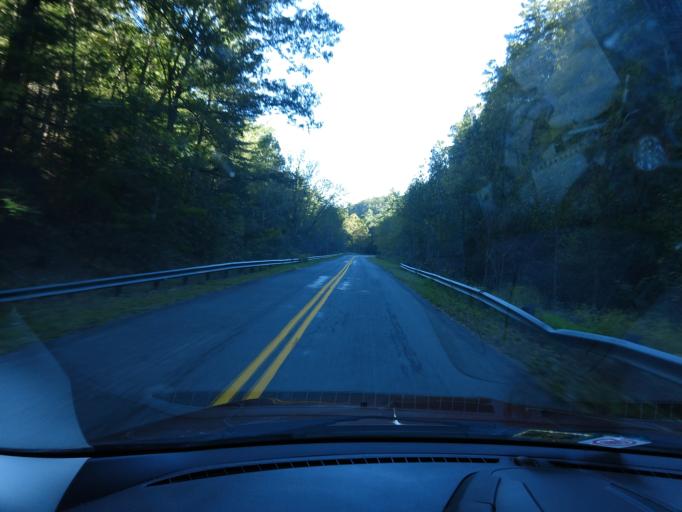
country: US
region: Virginia
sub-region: Alleghany County
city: Clifton Forge
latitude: 37.8338
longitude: -79.8434
